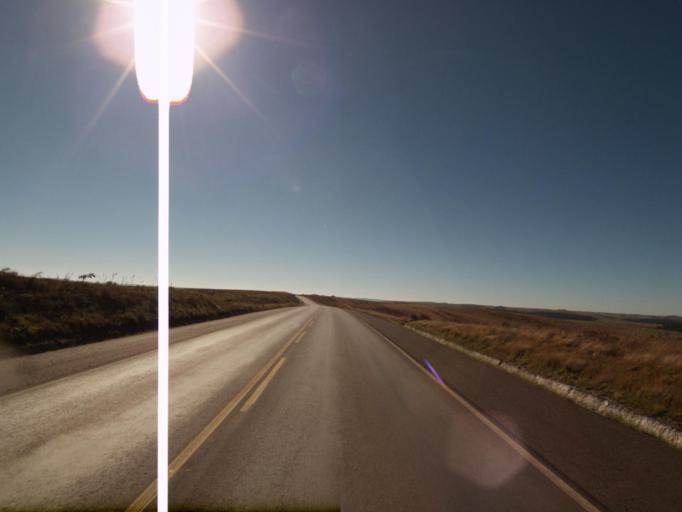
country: BR
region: Parana
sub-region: Palmas
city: Palmas
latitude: -26.7198
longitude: -51.6215
